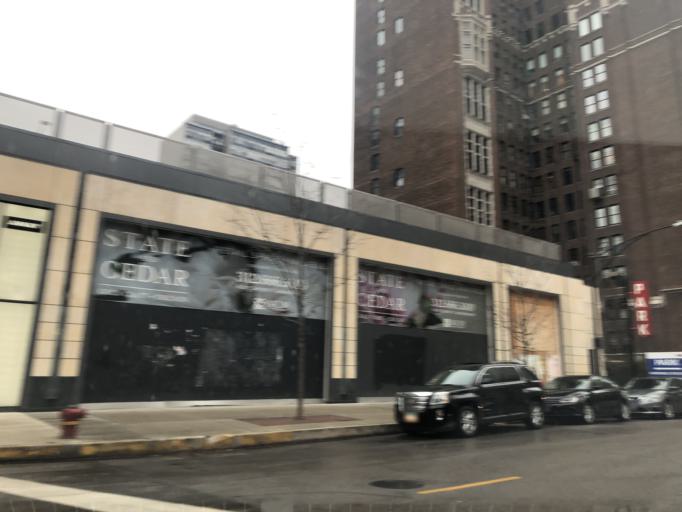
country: US
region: Illinois
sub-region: Cook County
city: Chicago
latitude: 41.9023
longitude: -87.6281
